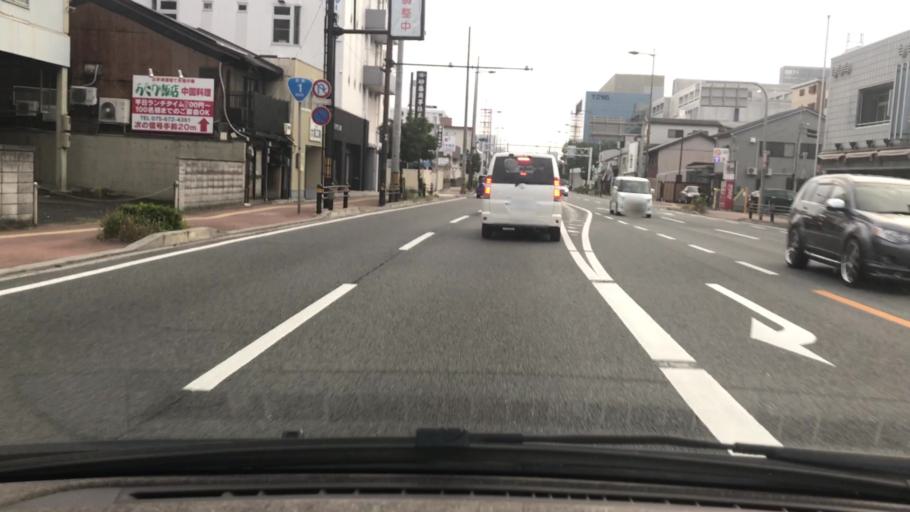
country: JP
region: Kyoto
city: Muko
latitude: 34.9729
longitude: 135.7461
